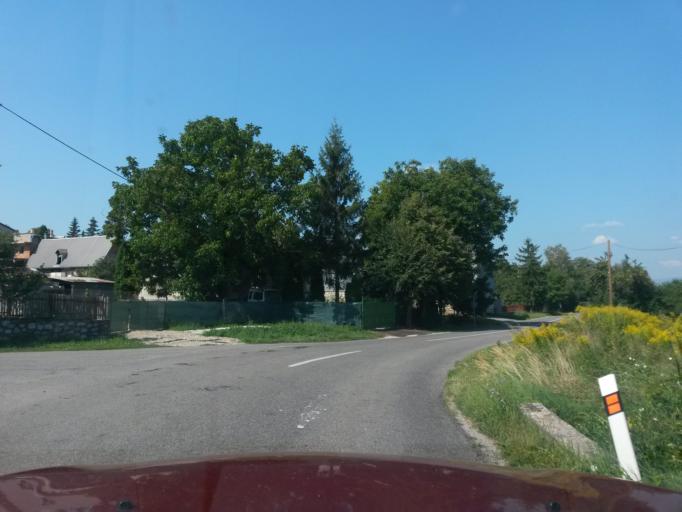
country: SK
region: Kosicky
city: Moldava nad Bodvou
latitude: 48.5308
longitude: 21.1263
